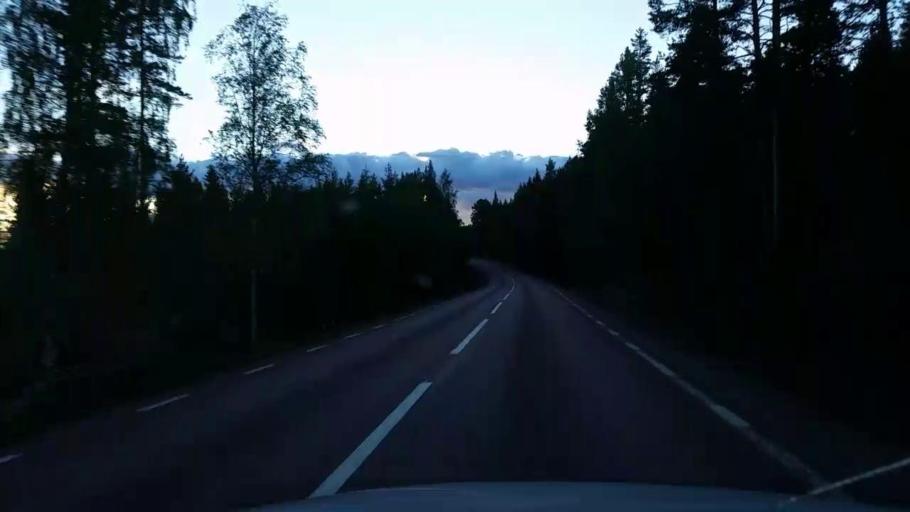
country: SE
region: Gaevleborg
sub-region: Ljusdals Kommun
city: Farila
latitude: 62.0973
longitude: 15.7924
